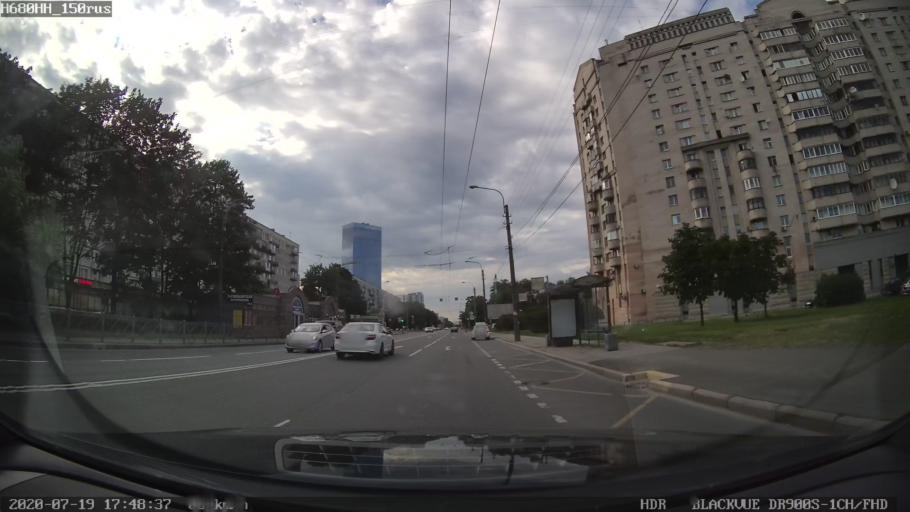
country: RU
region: St.-Petersburg
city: Kupchino
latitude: 59.8476
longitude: 30.3131
